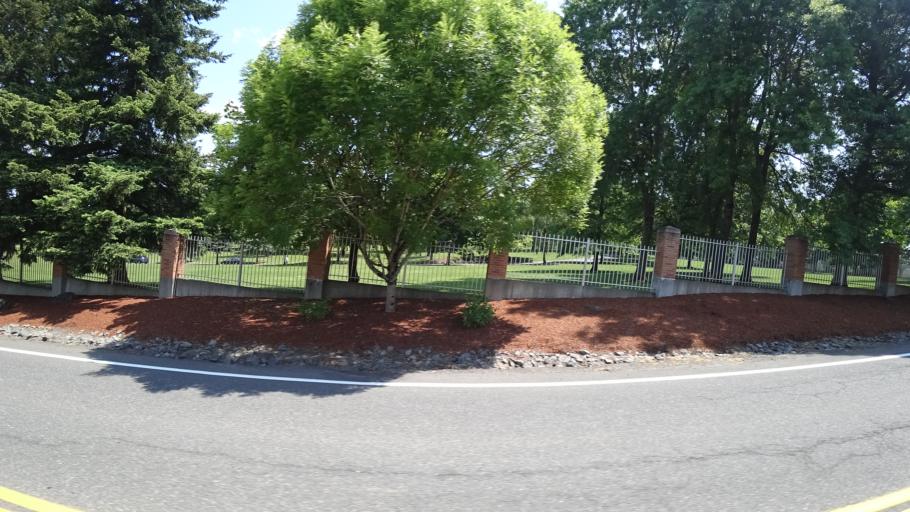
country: US
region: Oregon
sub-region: Clackamas County
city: Happy Valley
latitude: 45.4620
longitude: -122.5480
